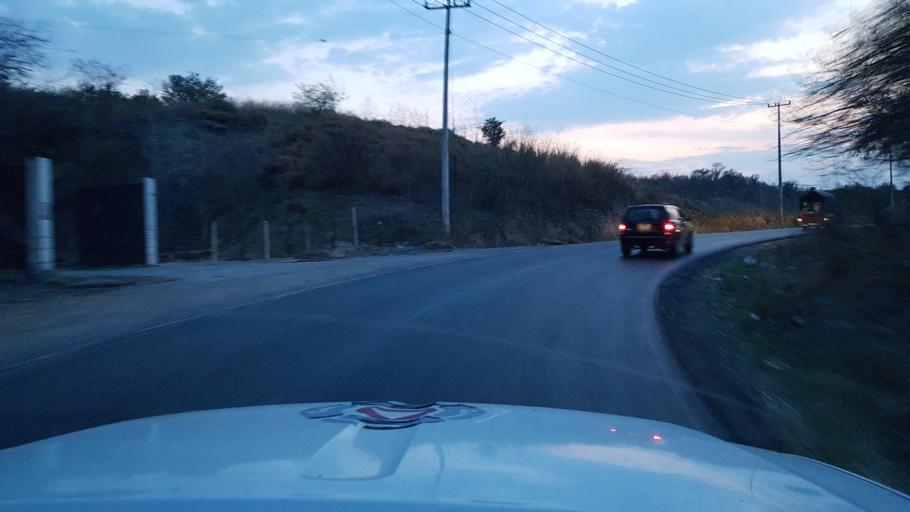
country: MX
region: Morelos
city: Tlaltizapan
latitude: 18.6890
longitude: -99.1405
